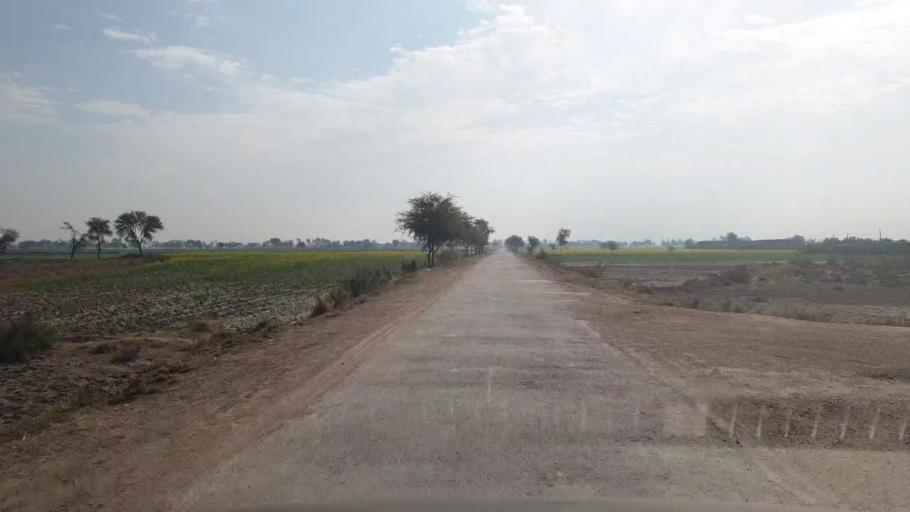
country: PK
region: Sindh
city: Hala
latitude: 25.9983
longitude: 68.4105
